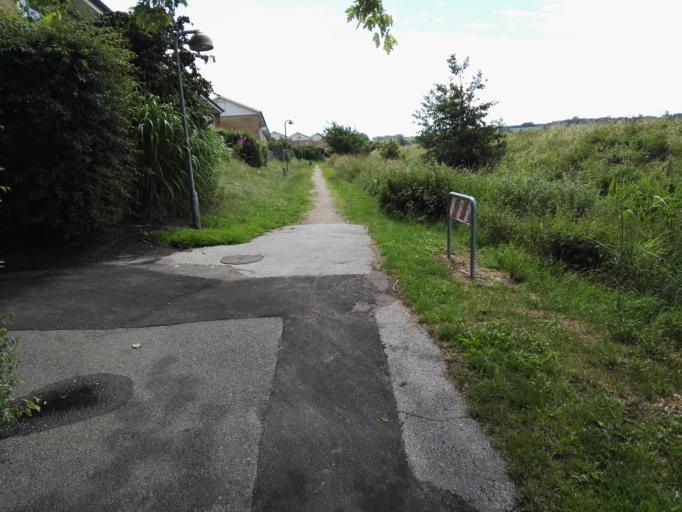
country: DK
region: Capital Region
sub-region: Frederikssund Kommune
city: Slangerup
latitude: 55.8401
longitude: 12.1814
